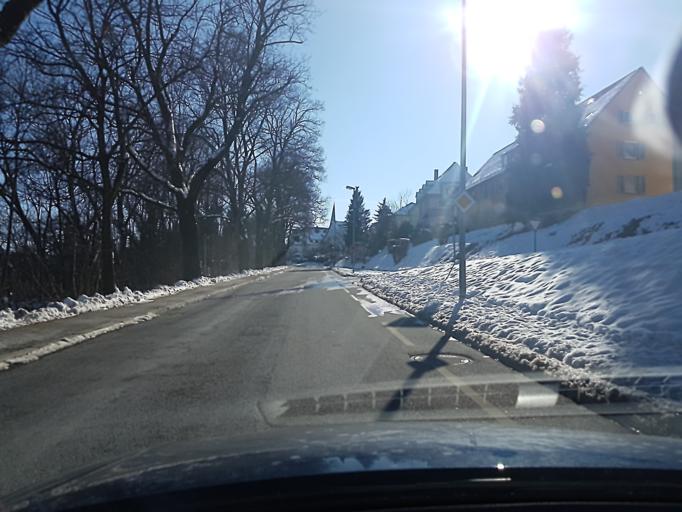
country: DE
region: Baden-Wuerttemberg
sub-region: Freiburg Region
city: Rottweil
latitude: 48.1728
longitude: 8.6266
